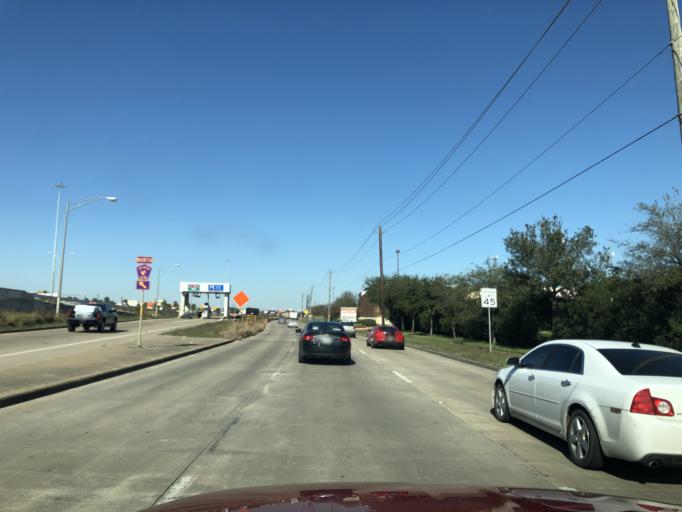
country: US
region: Texas
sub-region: Harris County
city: Deer Park
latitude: 29.6510
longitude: -95.1554
